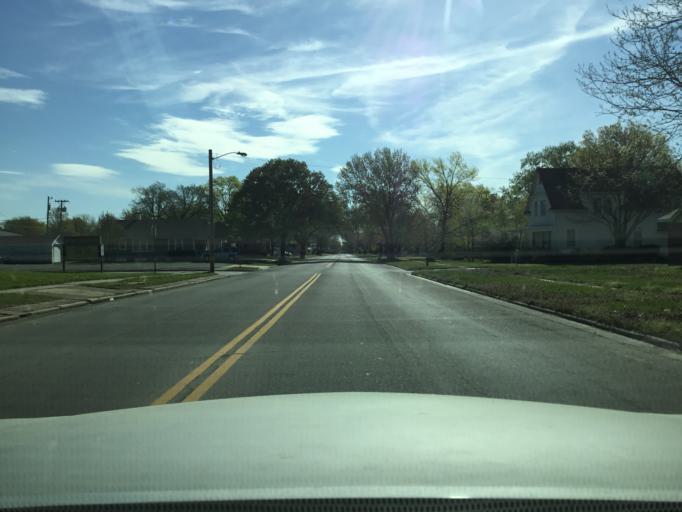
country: US
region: Kansas
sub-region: Neosho County
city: Chanute
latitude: 37.6820
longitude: -95.4691
